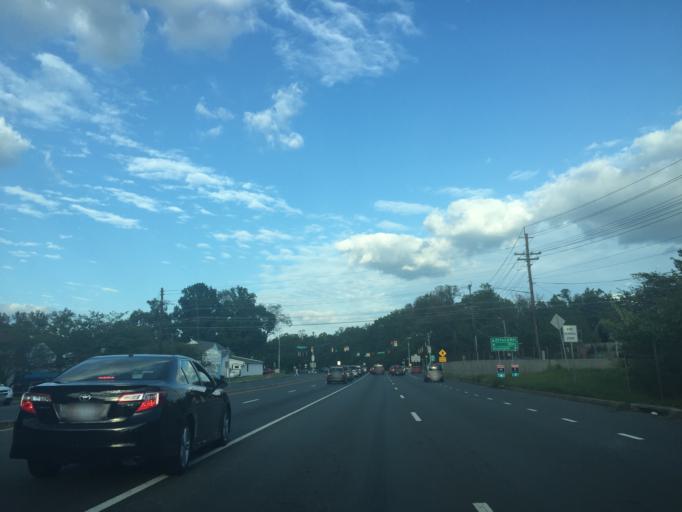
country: US
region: Maryland
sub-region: Montgomery County
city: Rossmoor
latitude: 39.1094
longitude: -77.0779
